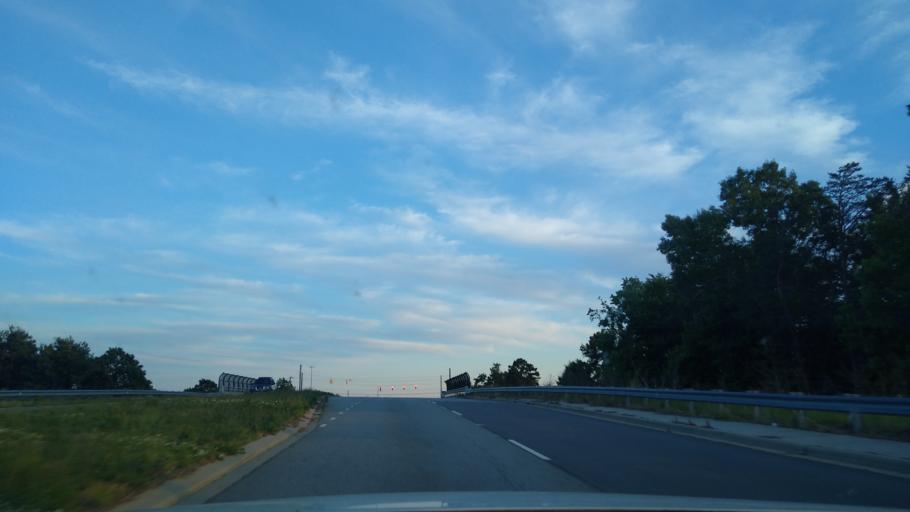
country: US
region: North Carolina
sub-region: Forsyth County
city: Kernersville
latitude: 36.1109
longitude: -80.0461
